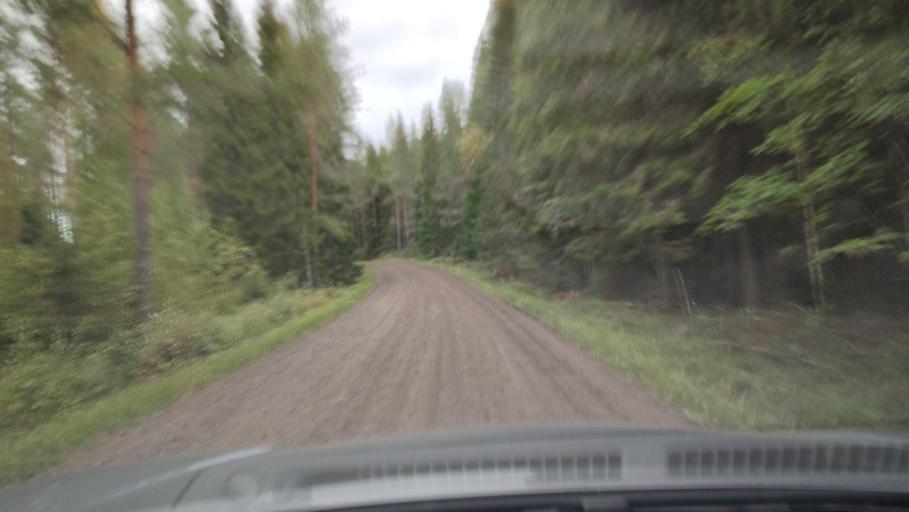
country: FI
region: Southern Ostrobothnia
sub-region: Suupohja
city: Karijoki
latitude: 62.2300
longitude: 21.5733
